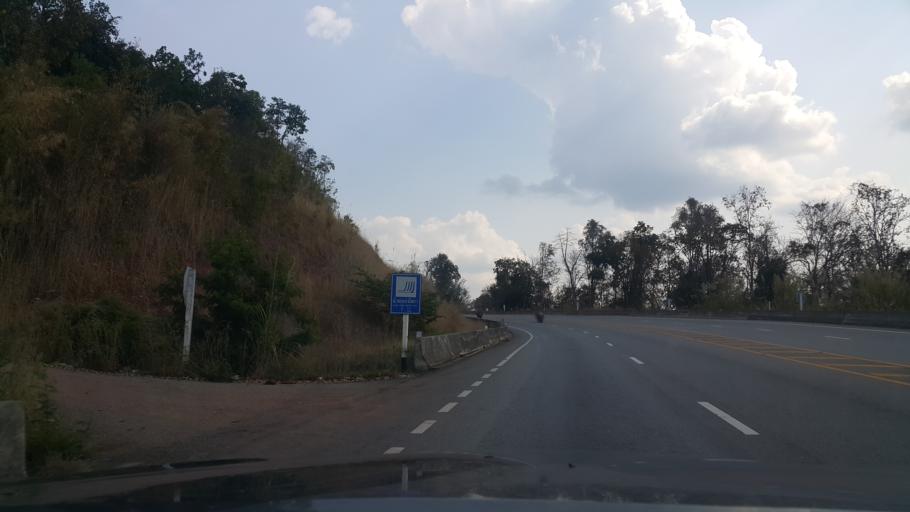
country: TH
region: Phitsanulok
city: Nakhon Thai
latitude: 16.8822
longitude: 100.8131
